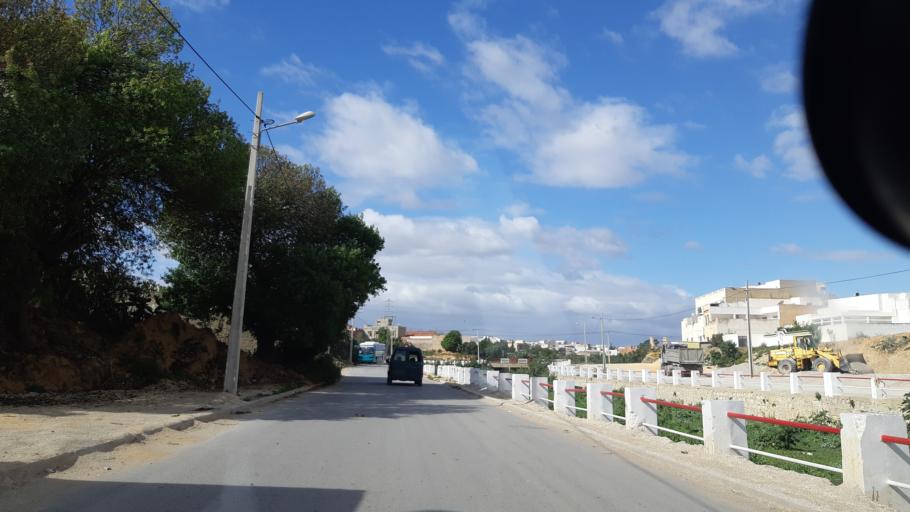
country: TN
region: Susah
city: Akouda
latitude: 35.8739
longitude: 10.5287
